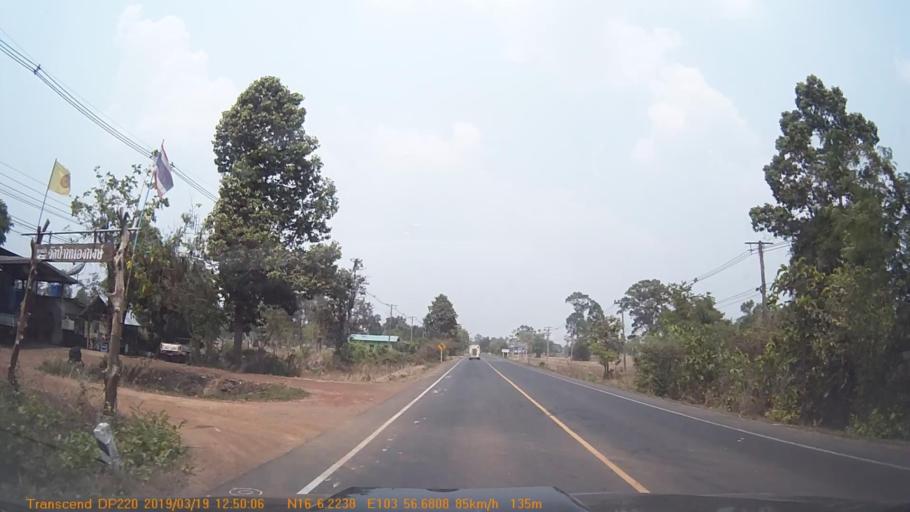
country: TH
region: Roi Et
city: Selaphum
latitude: 16.1041
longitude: 103.9447
